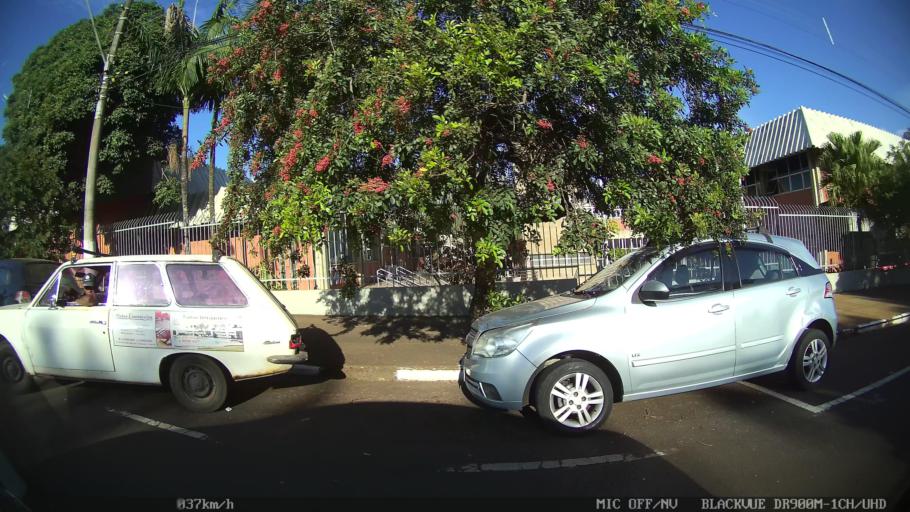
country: BR
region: Sao Paulo
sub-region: Franca
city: Franca
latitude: -20.5169
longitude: -47.3806
